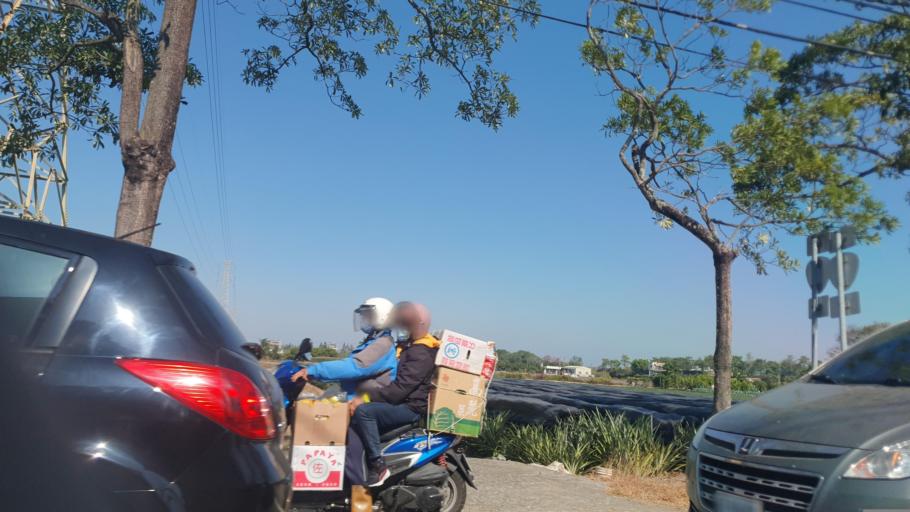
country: TW
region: Taiwan
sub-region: Tainan
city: Tainan
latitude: 23.0386
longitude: 120.3216
